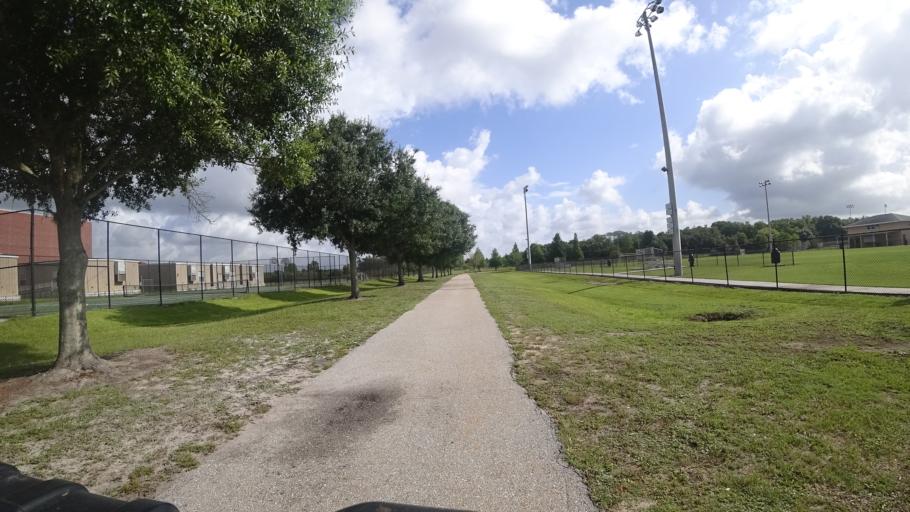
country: US
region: Florida
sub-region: Manatee County
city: Ellenton
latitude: 27.5759
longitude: -82.4874
